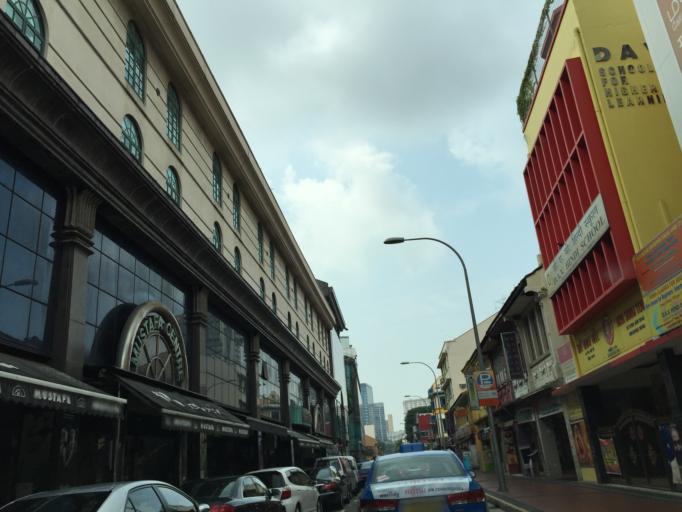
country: SG
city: Singapore
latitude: 1.3100
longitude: 103.8551
